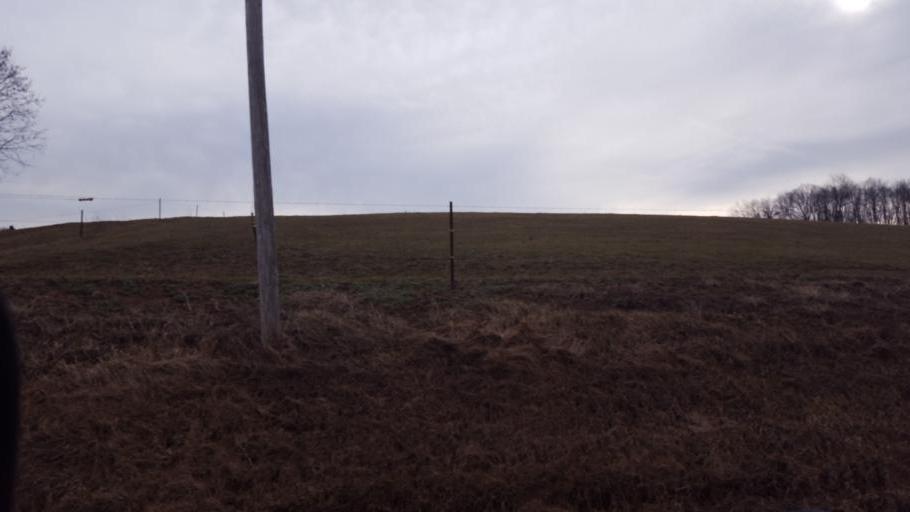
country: US
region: Ohio
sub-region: Knox County
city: Danville
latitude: 40.5271
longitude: -82.3002
